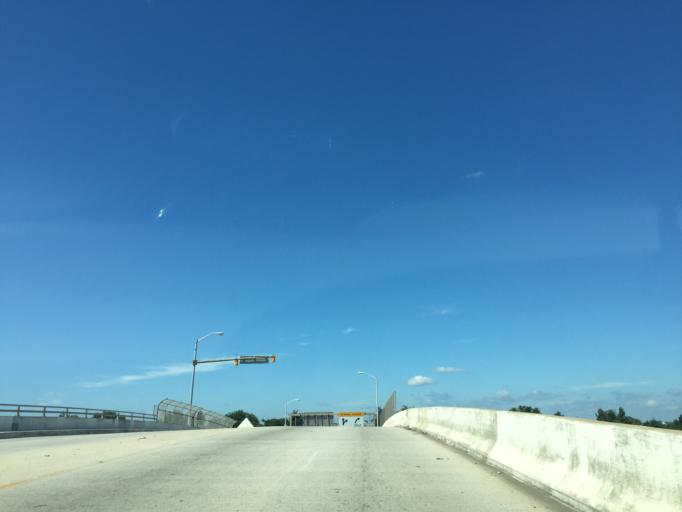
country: US
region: Maryland
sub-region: Baltimore County
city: Rosedale
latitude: 39.2919
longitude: -76.5567
